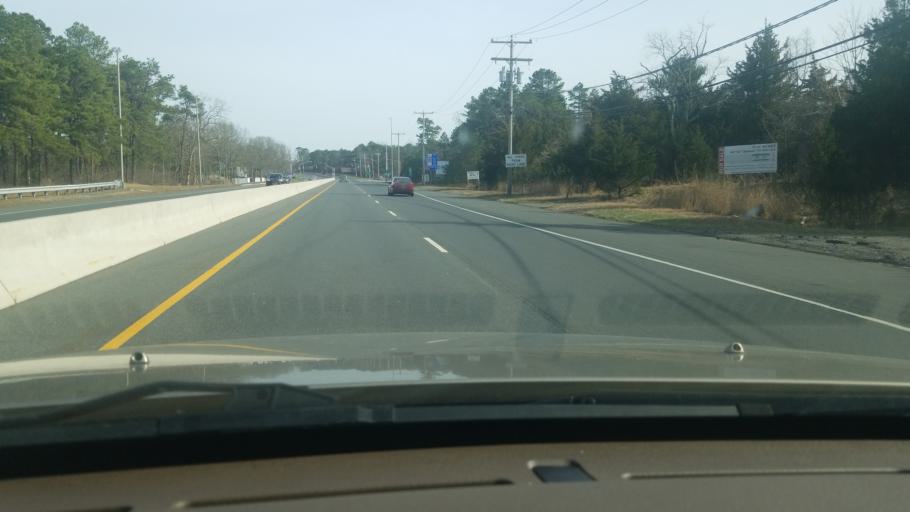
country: US
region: New Jersey
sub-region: Ocean County
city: Lakehurst
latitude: 40.0080
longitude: -74.2998
